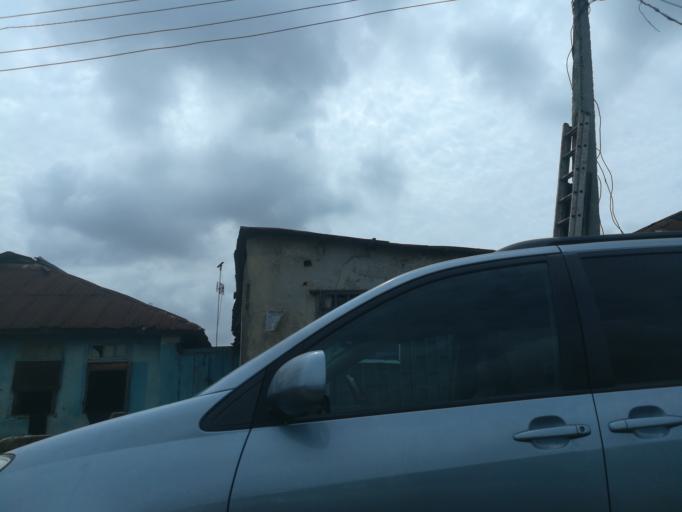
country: NG
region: Lagos
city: Somolu
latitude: 6.5454
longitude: 3.3947
